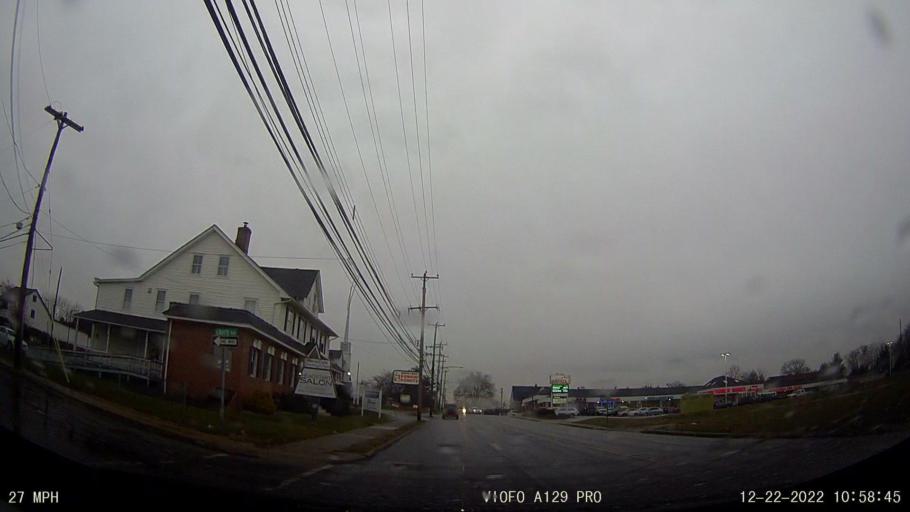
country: US
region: Pennsylvania
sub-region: Montgomery County
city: West Norriton
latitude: 40.1321
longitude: -75.3773
